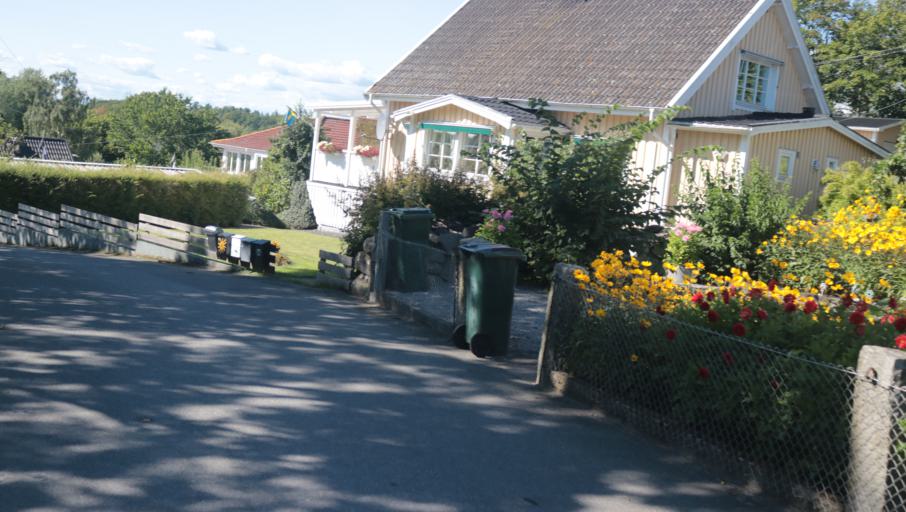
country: SE
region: Blekinge
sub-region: Karlshamns Kommun
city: Karlshamn
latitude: 56.1605
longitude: 14.8547
